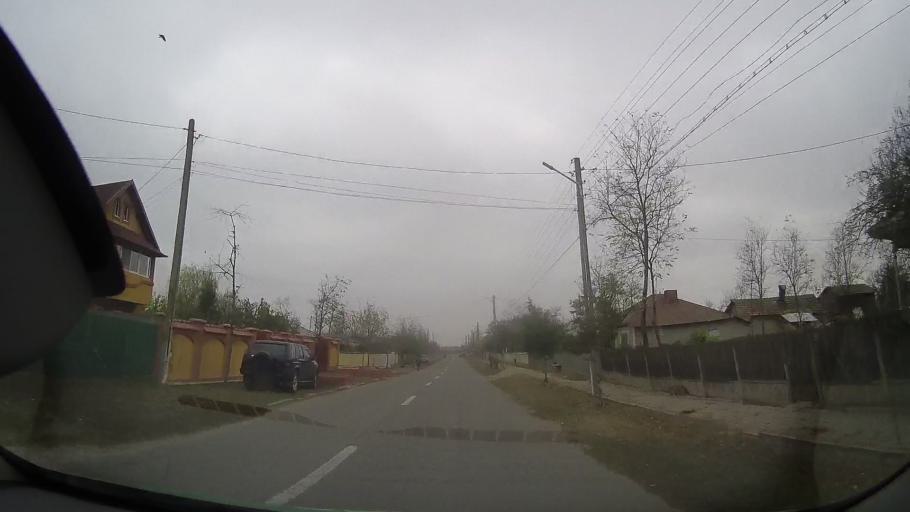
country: RO
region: Ialomita
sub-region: Comuna Grindu
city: Grindu
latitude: 44.7684
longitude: 26.9057
